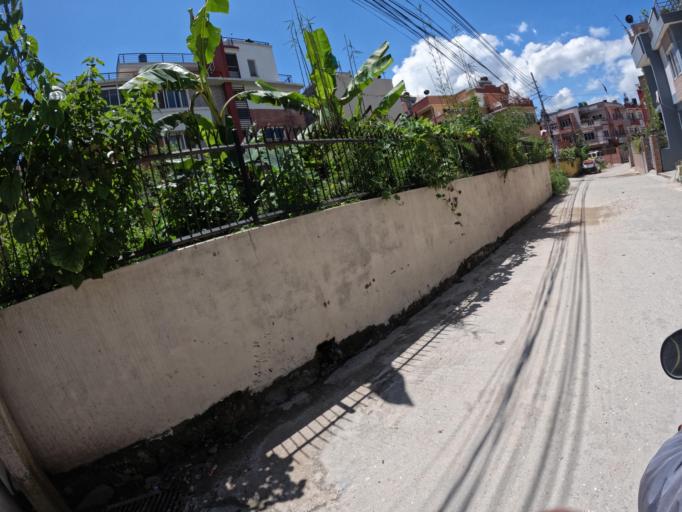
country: NP
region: Central Region
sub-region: Bagmati Zone
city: Kathmandu
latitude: 27.7506
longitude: 85.3303
